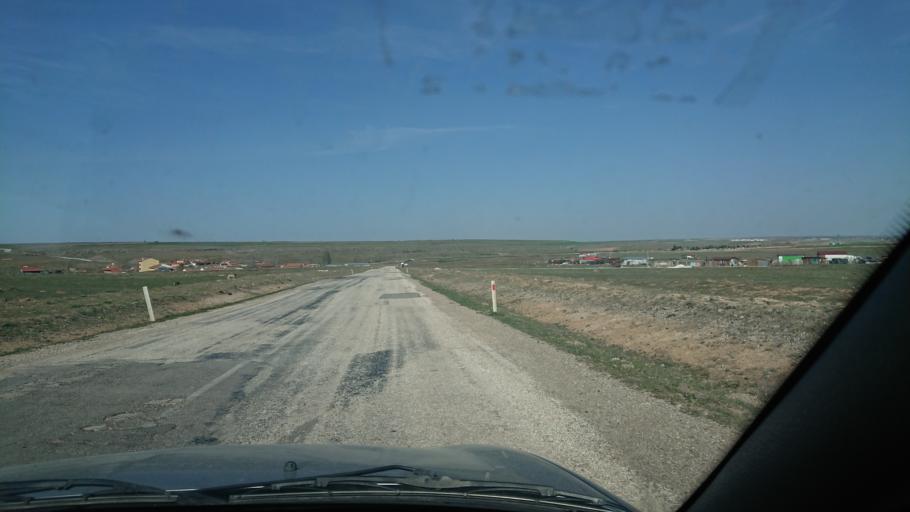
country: TR
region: Eskisehir
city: Eskisehir
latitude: 39.6729
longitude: 30.4789
